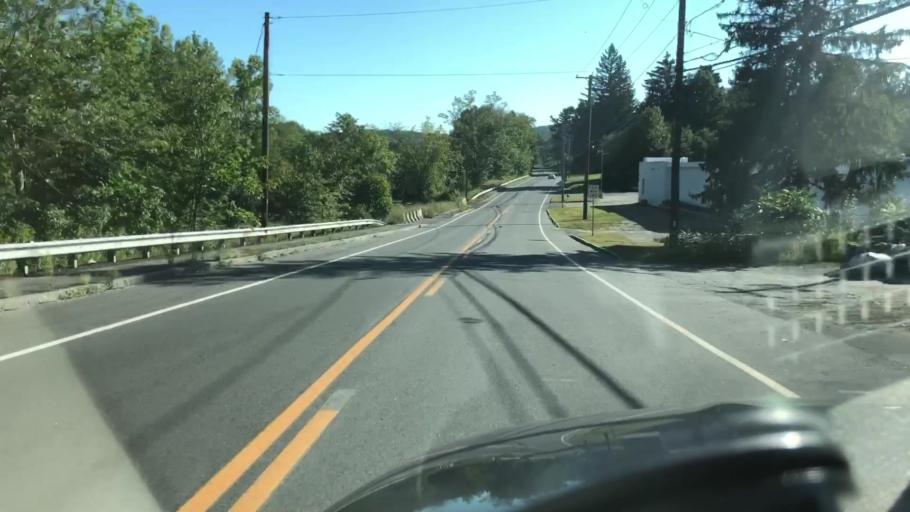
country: US
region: Massachusetts
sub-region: Hampden County
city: Monson
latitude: 42.1233
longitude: -72.3081
